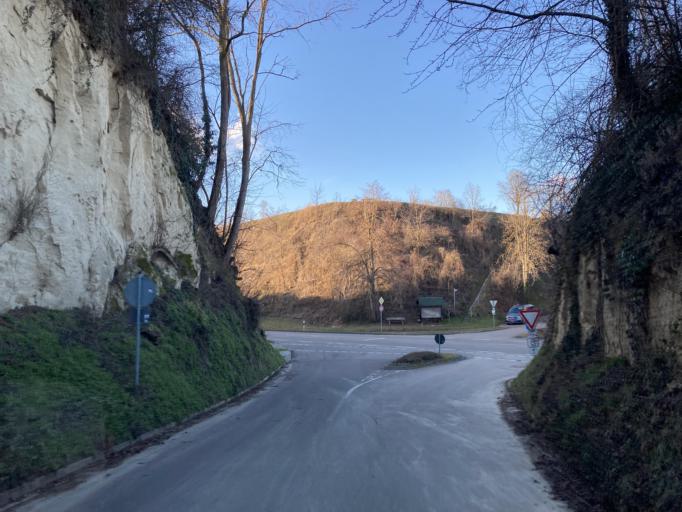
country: DE
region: Baden-Wuerttemberg
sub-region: Freiburg Region
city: Merdingen
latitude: 48.0123
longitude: 7.6983
